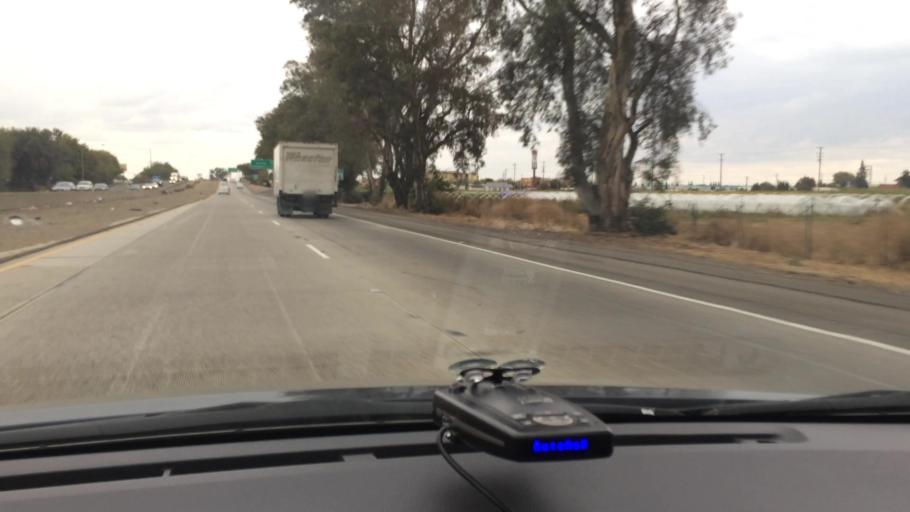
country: US
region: California
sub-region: San Joaquin County
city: Lodi
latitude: 38.1117
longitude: -121.2588
